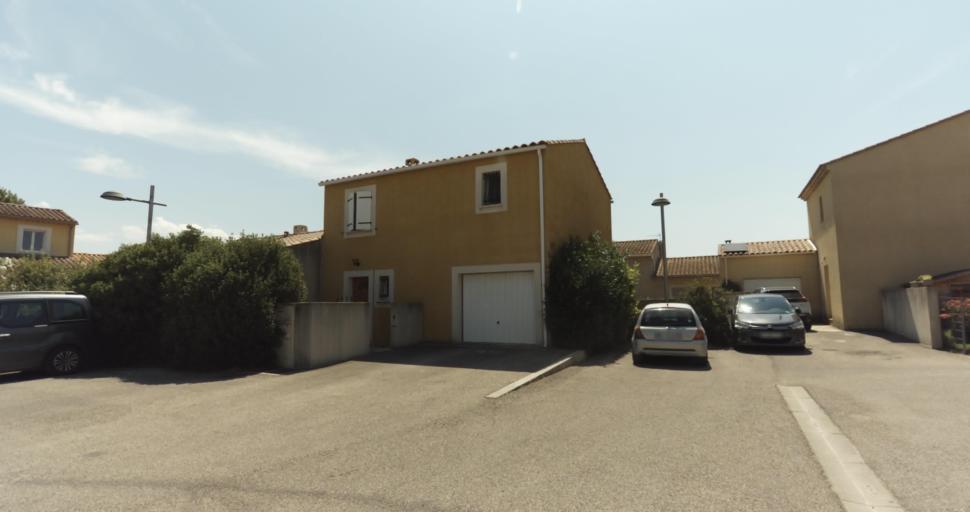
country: FR
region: Provence-Alpes-Cote d'Azur
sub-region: Departement du Vaucluse
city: Monteux
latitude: 44.0298
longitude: 4.9911
